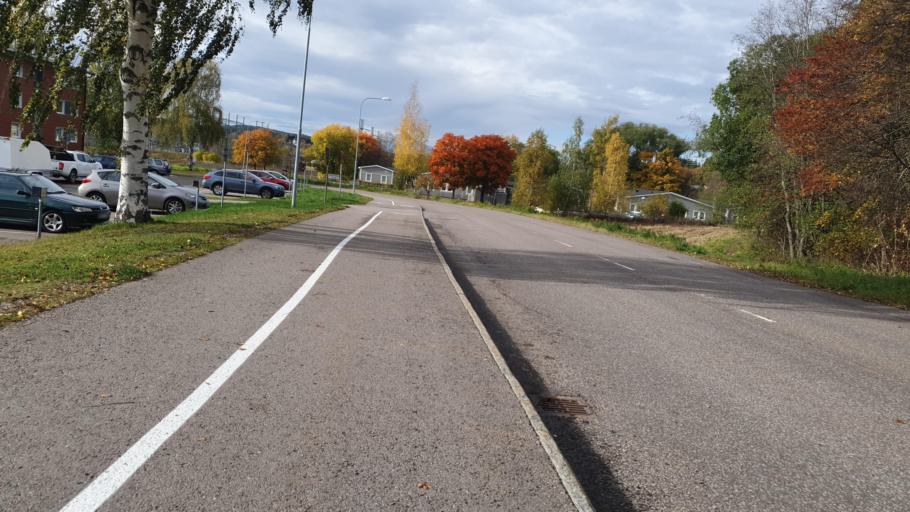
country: SE
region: Vaesternorrland
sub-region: Sundsvalls Kommun
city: Sundsvall
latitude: 62.4069
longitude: 17.2477
